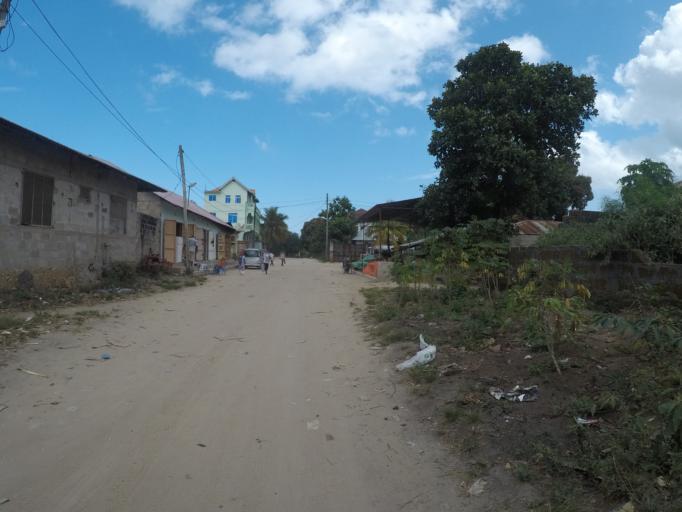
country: TZ
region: Zanzibar Urban/West
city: Zanzibar
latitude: -6.1875
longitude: 39.2172
